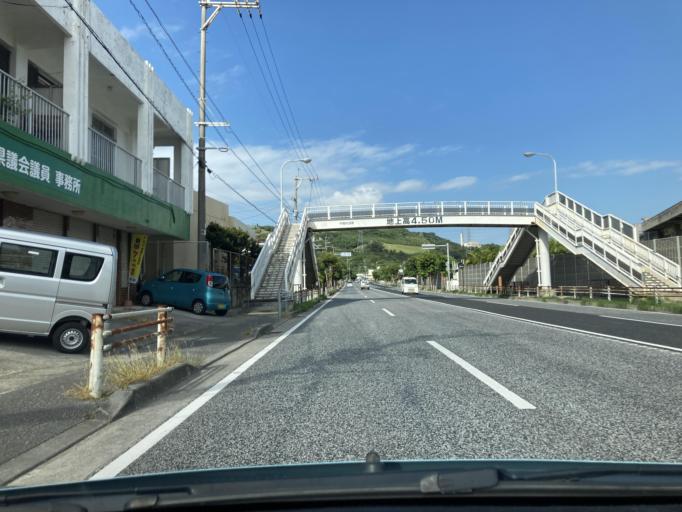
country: JP
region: Okinawa
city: Ginowan
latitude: 26.2681
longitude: 127.7909
